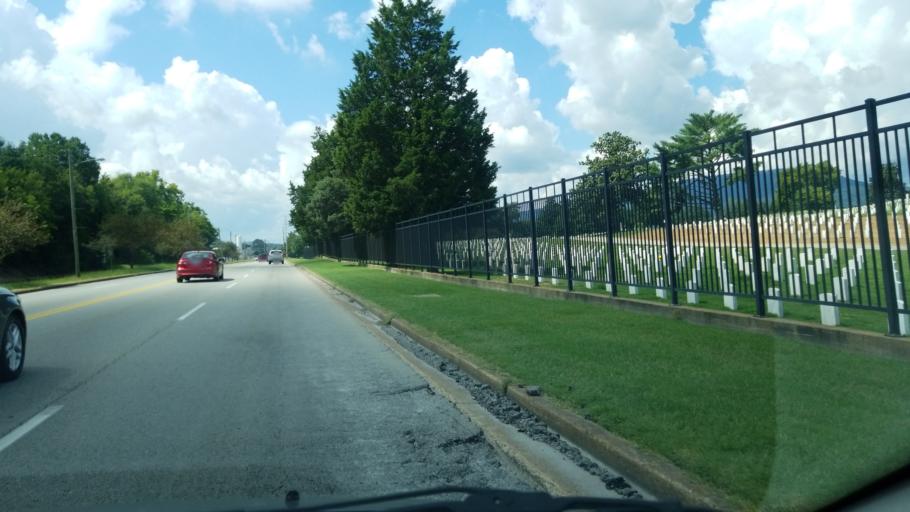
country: US
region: Tennessee
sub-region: Hamilton County
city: Chattanooga
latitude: 35.0350
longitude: -85.2851
